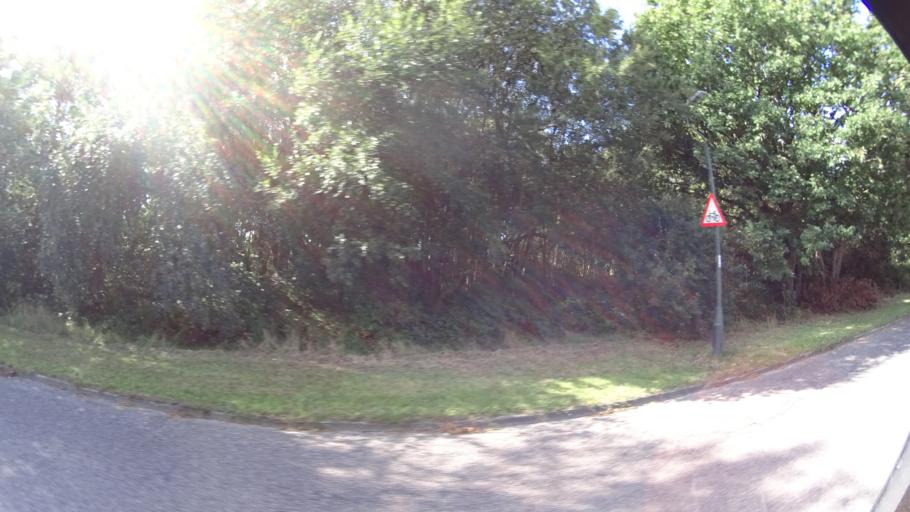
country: GB
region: England
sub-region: Dorset
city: Parkstone
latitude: 50.7543
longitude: -1.9175
